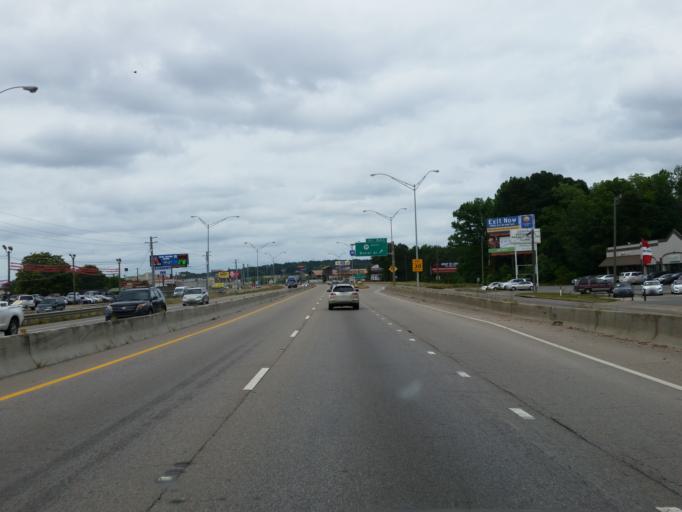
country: US
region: Mississippi
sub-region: Lauderdale County
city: Meridian
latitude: 32.3593
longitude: -88.6818
